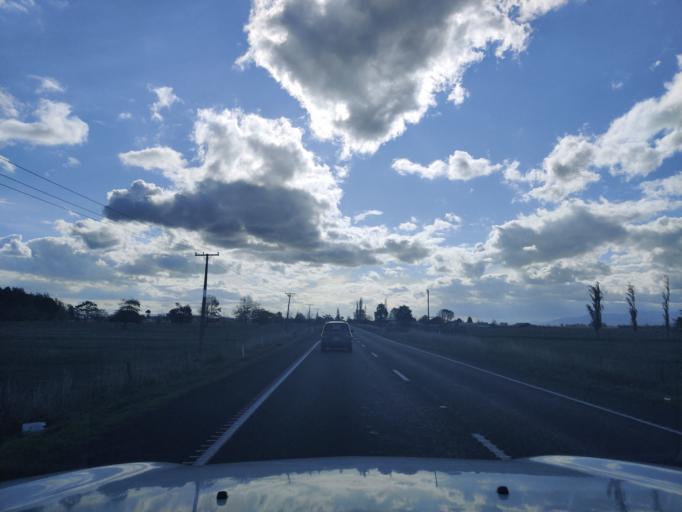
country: NZ
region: Waikato
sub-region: Hauraki District
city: Ngatea
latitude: -37.2915
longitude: 175.5503
